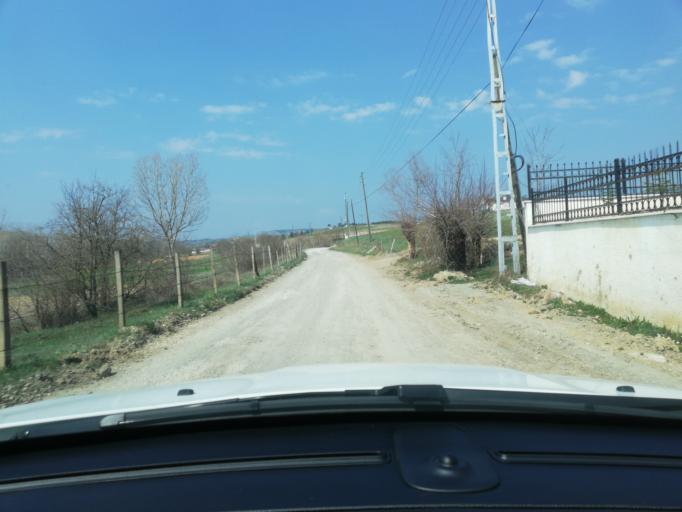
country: TR
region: Kastamonu
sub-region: Cide
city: Kastamonu
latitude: 41.4601
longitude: 33.7558
